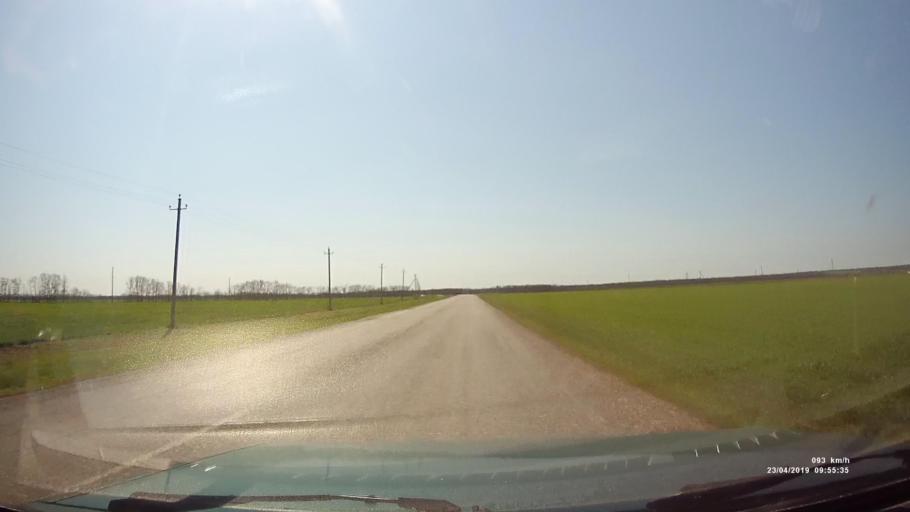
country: RU
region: Rostov
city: Orlovskiy
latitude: 46.8070
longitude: 42.0639
